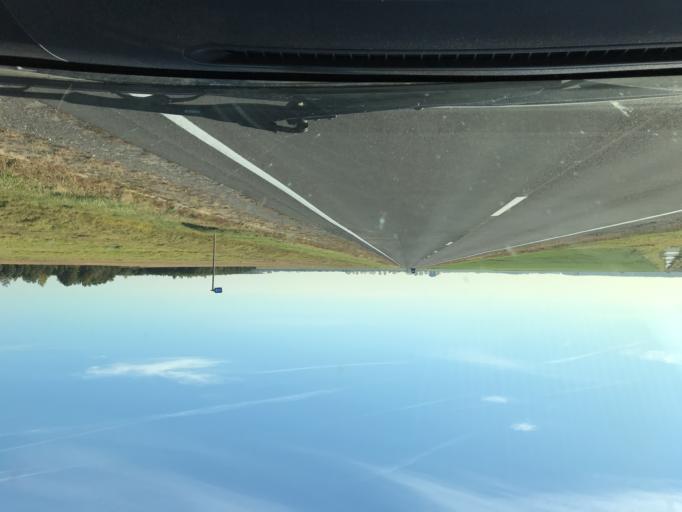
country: BY
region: Brest
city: Antopal'
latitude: 52.2230
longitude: 24.8320
